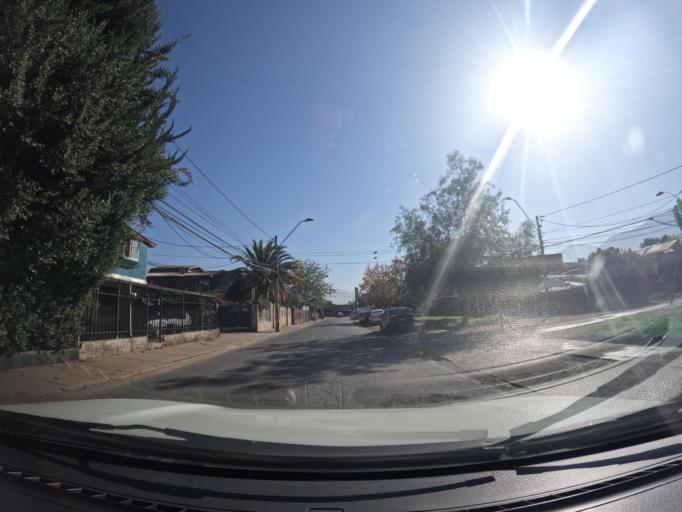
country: CL
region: Santiago Metropolitan
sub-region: Provincia de Santiago
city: Villa Presidente Frei, Nunoa, Santiago, Chile
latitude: -33.4774
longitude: -70.5723
